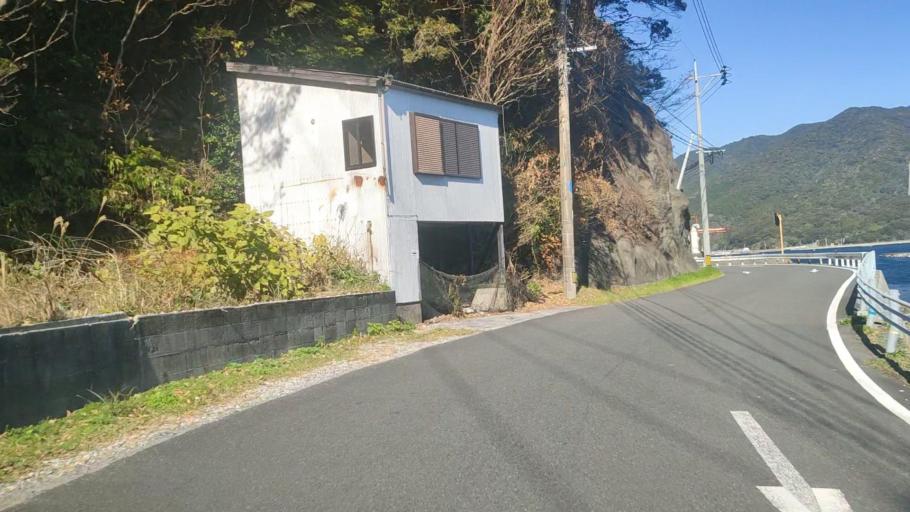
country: JP
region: Oita
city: Saiki
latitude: 32.8355
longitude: 131.9581
